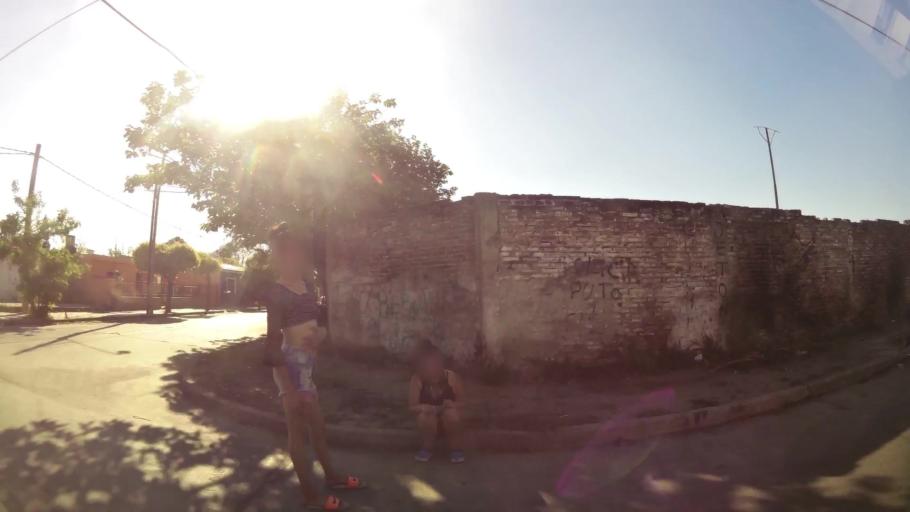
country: AR
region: Cordoba
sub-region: Departamento de Capital
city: Cordoba
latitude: -31.3866
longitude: -64.1657
